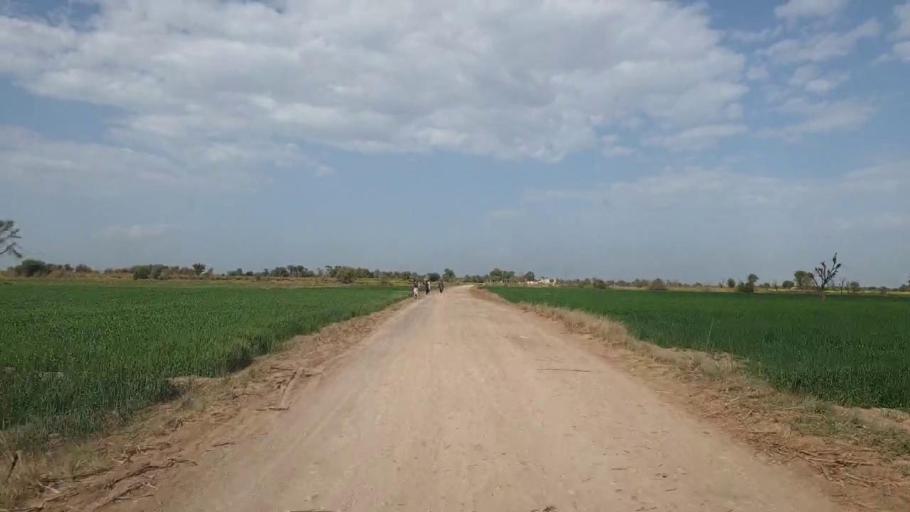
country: PK
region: Sindh
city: Shahdadpur
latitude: 25.9774
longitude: 68.4770
